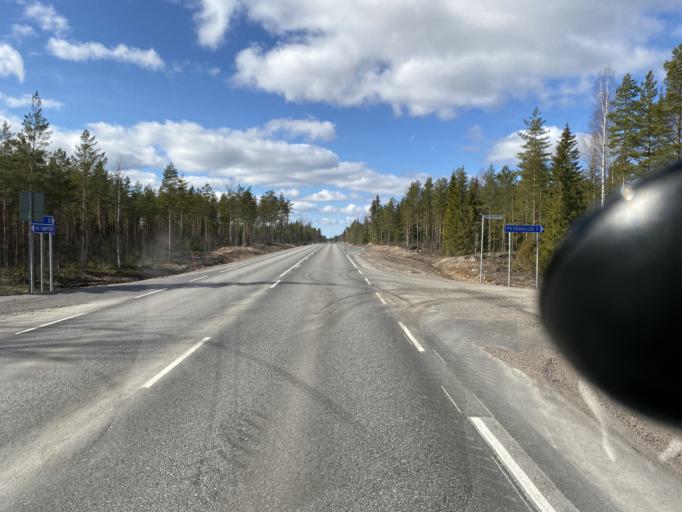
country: FI
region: Satakunta
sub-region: Pori
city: Kokemaeki
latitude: 61.1668
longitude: 22.4270
